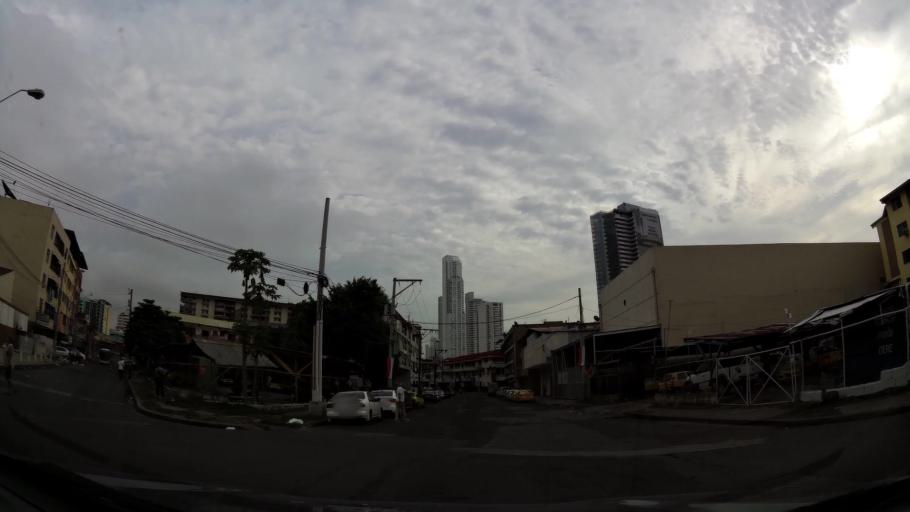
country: PA
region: Panama
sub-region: Distrito de Panama
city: Ancon
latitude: 8.9631
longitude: -79.5389
